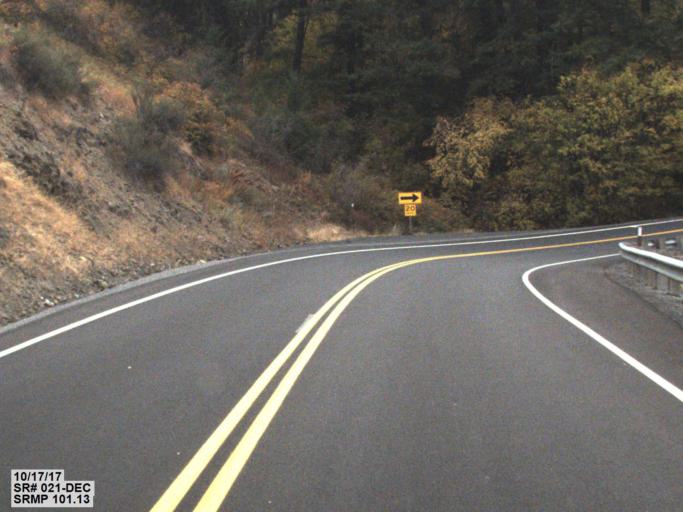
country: US
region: Washington
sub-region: Okanogan County
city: Coulee Dam
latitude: 47.8715
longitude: -118.7194
